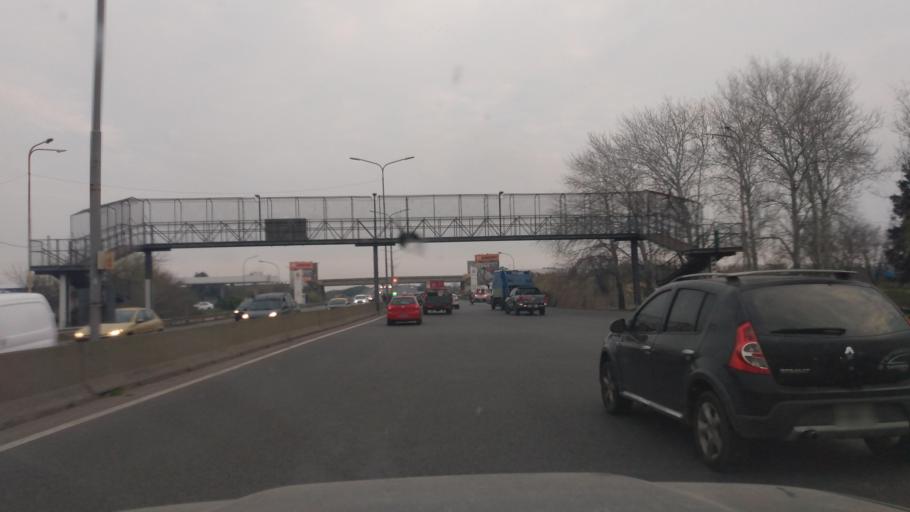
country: AR
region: Buenos Aires
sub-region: Partido de Tigre
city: Tigre
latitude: -34.5042
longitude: -58.5896
